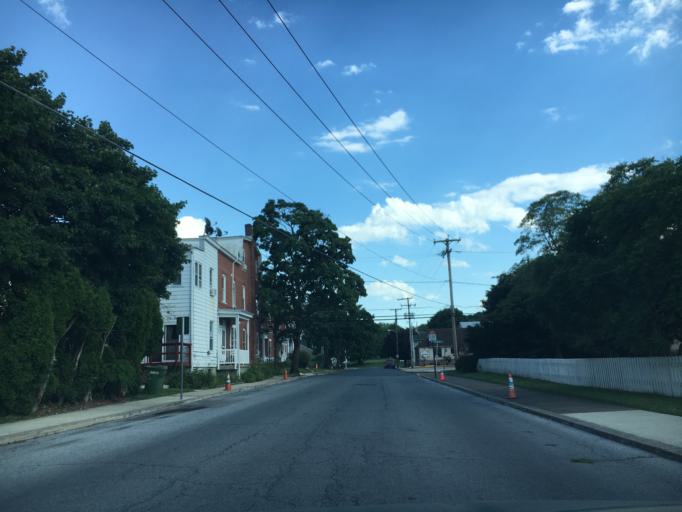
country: US
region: Pennsylvania
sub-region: Berks County
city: Fleetwood
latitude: 40.4537
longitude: -75.8233
